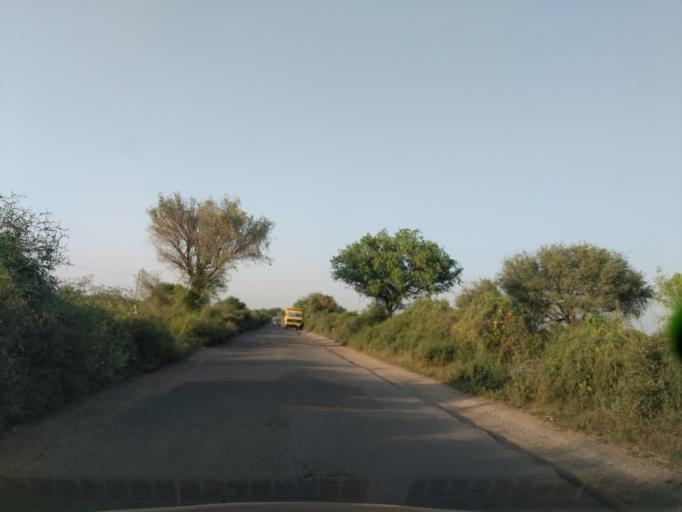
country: IN
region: Rajasthan
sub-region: Churu
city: Rajgarh
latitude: 28.5809
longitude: 75.3725
